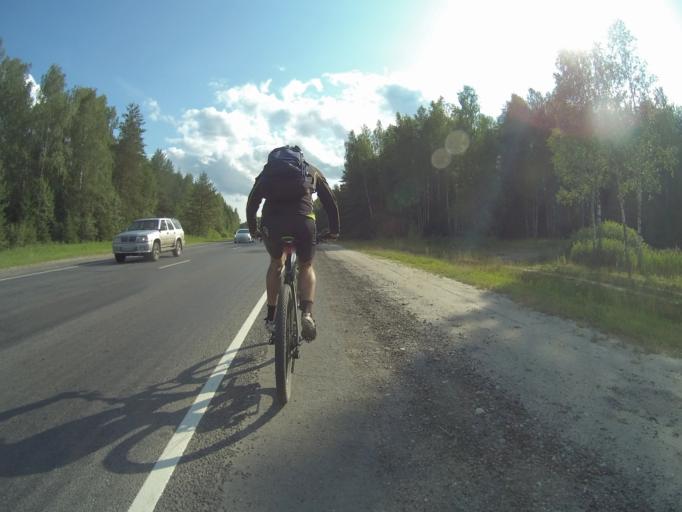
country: RU
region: Ivanovo
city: Novoye Leushino
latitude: 56.6827
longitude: 40.6064
